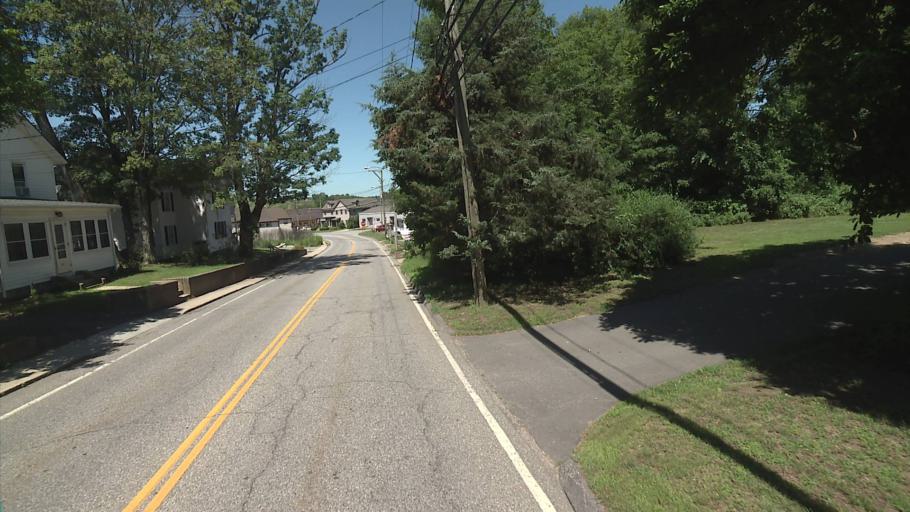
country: US
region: Connecticut
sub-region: New London County
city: Colchester
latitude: 41.5799
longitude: -72.3249
